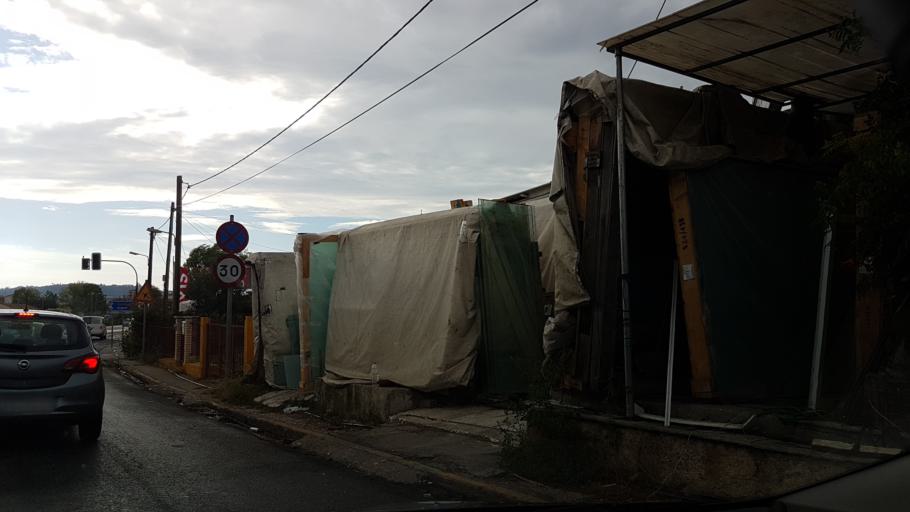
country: GR
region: Ionian Islands
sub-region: Nomos Kerkyras
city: Kerkyra
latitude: 39.6132
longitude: 19.9110
